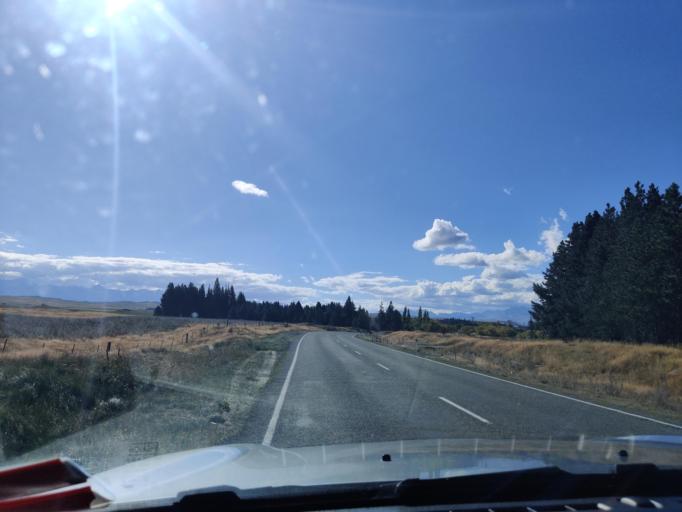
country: NZ
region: Canterbury
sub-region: Timaru District
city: Pleasant Point
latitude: -44.0899
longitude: 170.3498
